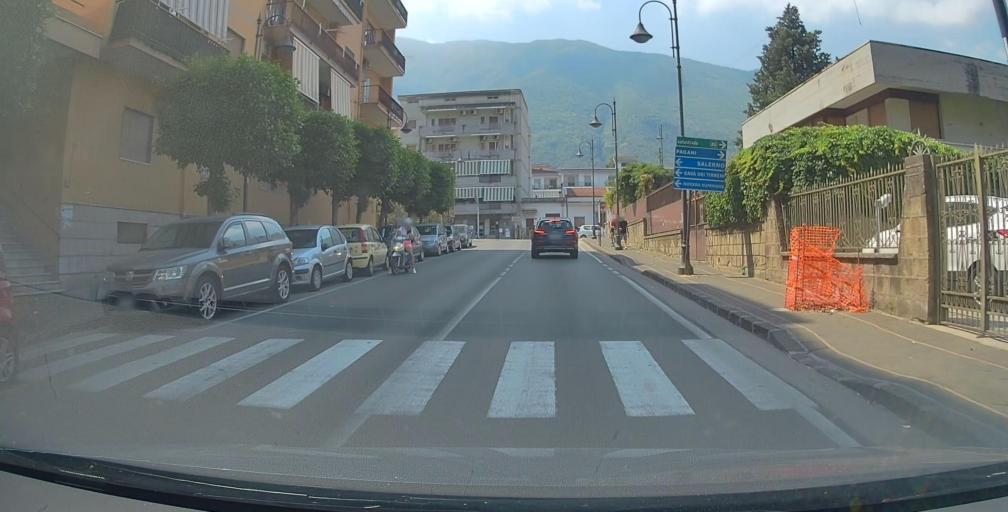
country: IT
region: Campania
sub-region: Provincia di Salerno
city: Nocera Inferiore
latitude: 40.7418
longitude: 14.6496
